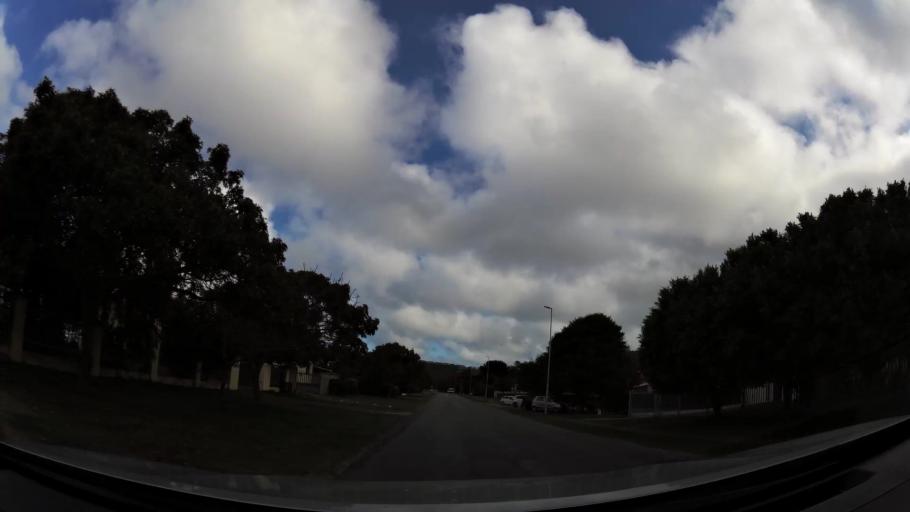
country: ZA
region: Western Cape
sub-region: Eden District Municipality
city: Plettenberg Bay
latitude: -34.0765
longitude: 23.3653
